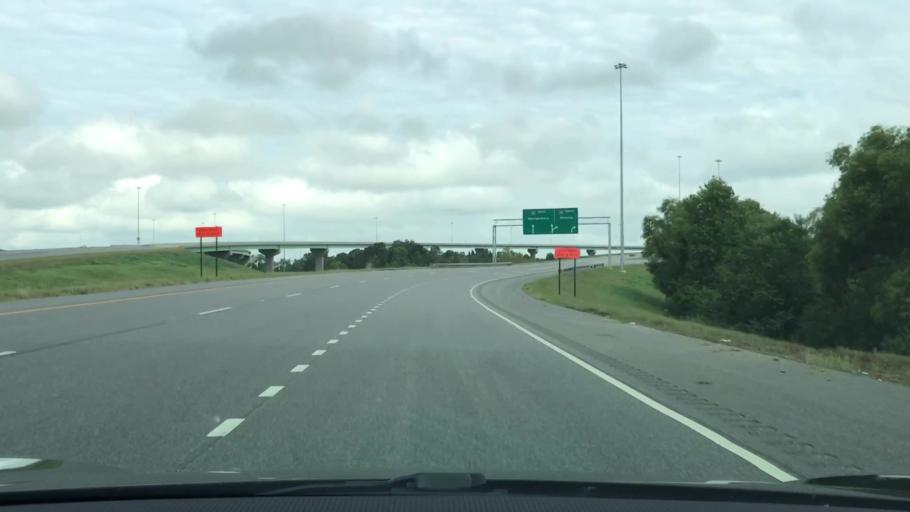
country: US
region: Alabama
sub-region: Montgomery County
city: Pike Road
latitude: 32.3623
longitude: -86.0768
